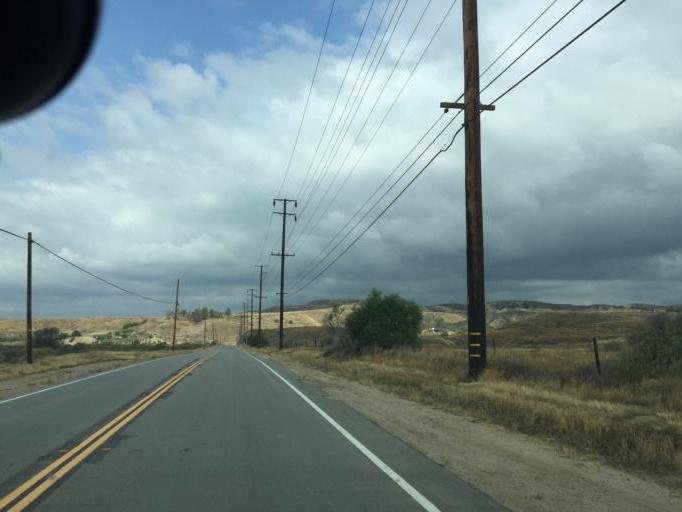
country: US
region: California
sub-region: Los Angeles County
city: Santa Clarita
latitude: 34.4738
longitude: -118.4587
